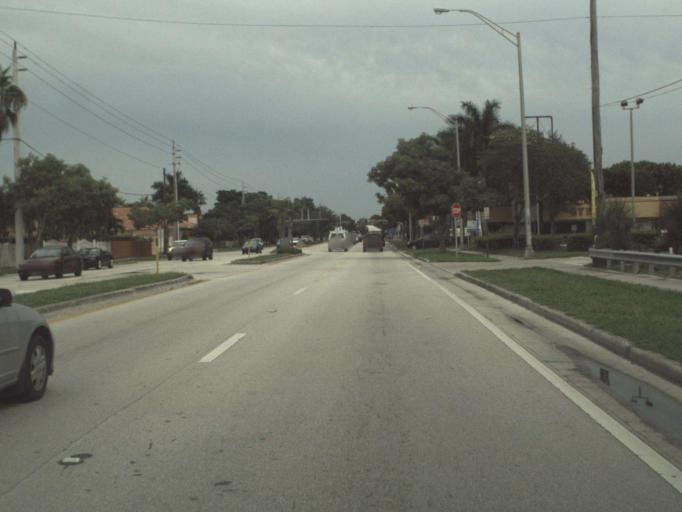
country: US
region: Florida
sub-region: Miami-Dade County
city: Palm Springs North
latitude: 25.9423
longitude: -80.3262
